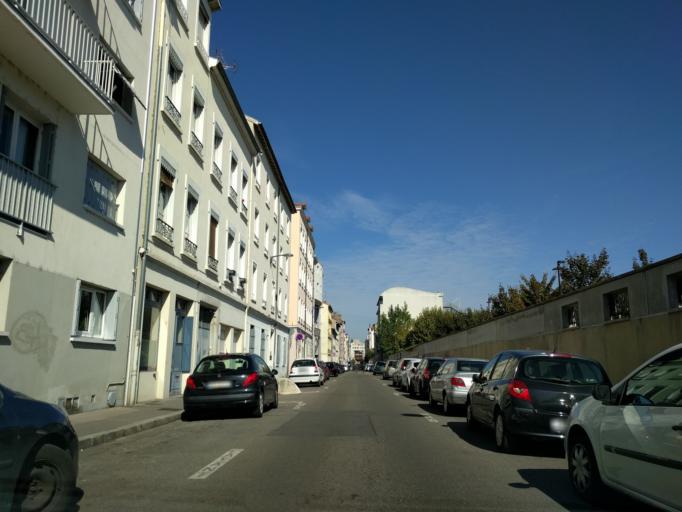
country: FR
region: Rhone-Alpes
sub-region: Departement du Rhone
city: Villeurbanne
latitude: 45.7670
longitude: 4.8689
